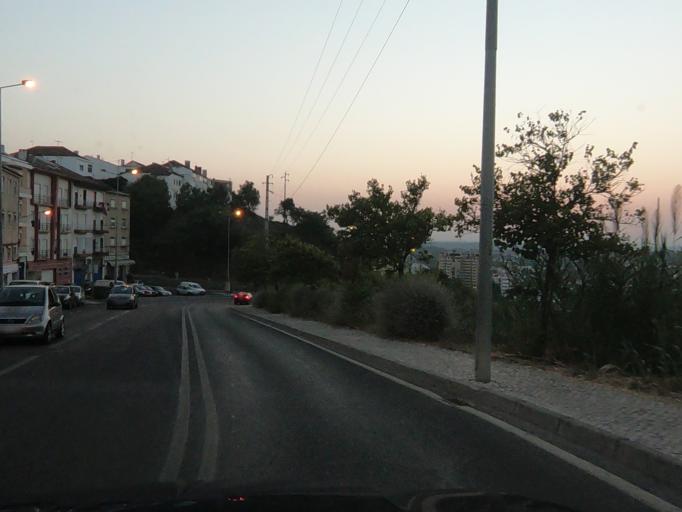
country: PT
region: Santarem
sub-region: Santarem
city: Santarem
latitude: 39.2381
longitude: -8.6901
